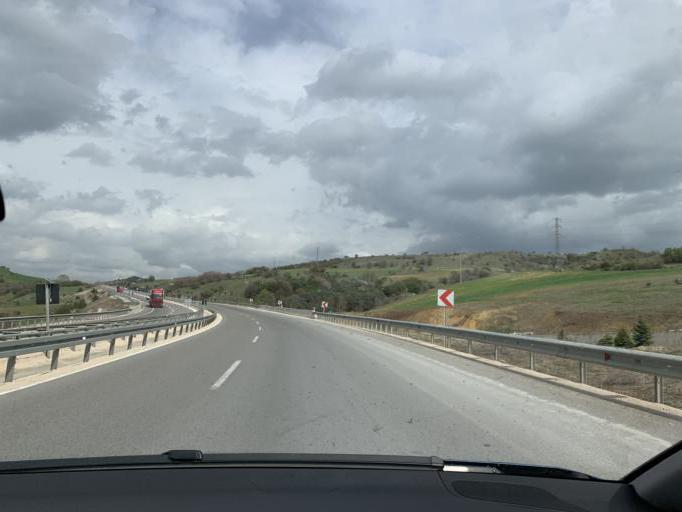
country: TR
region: Bolu
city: Yenicaga
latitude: 40.7802
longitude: 32.0916
